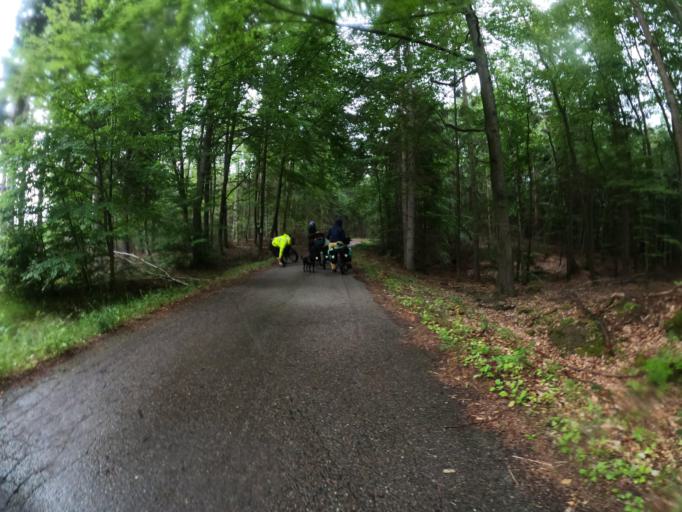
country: PL
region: West Pomeranian Voivodeship
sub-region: Powiat szczecinecki
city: Grzmiaca
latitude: 53.7173
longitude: 16.4976
